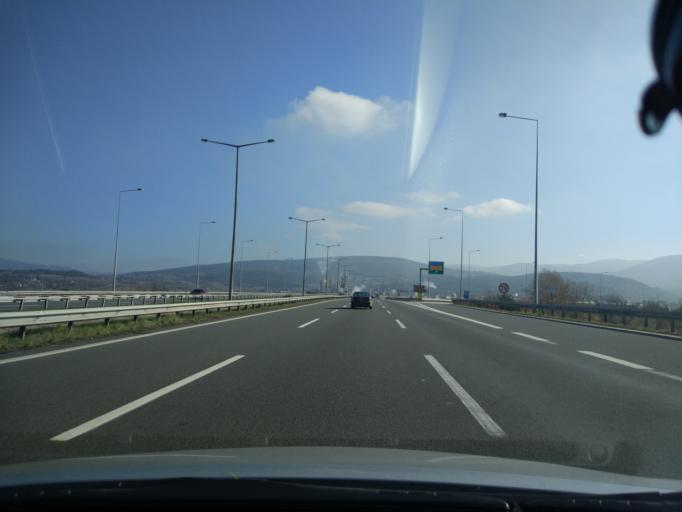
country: TR
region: Bolu
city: Bolu
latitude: 40.7614
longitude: 31.7625
